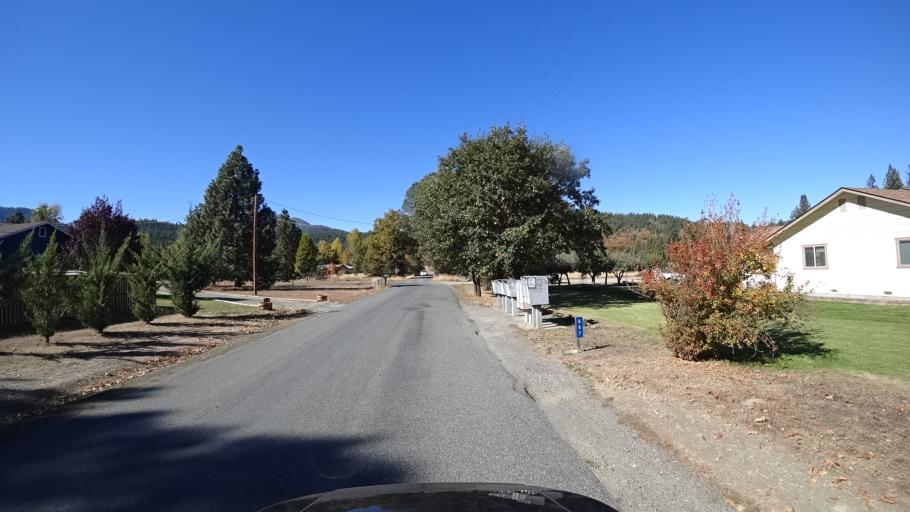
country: US
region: California
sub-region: Siskiyou County
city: Yreka
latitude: 41.5267
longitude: -122.9186
